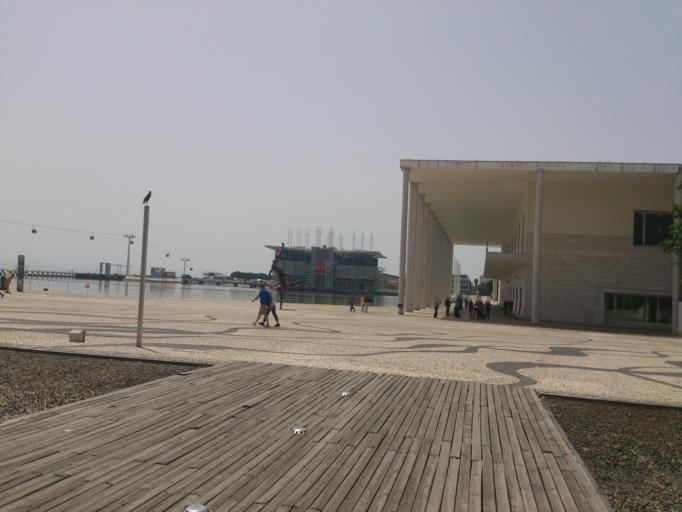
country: PT
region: Lisbon
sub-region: Loures
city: Moscavide
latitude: 38.7675
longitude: -9.0946
